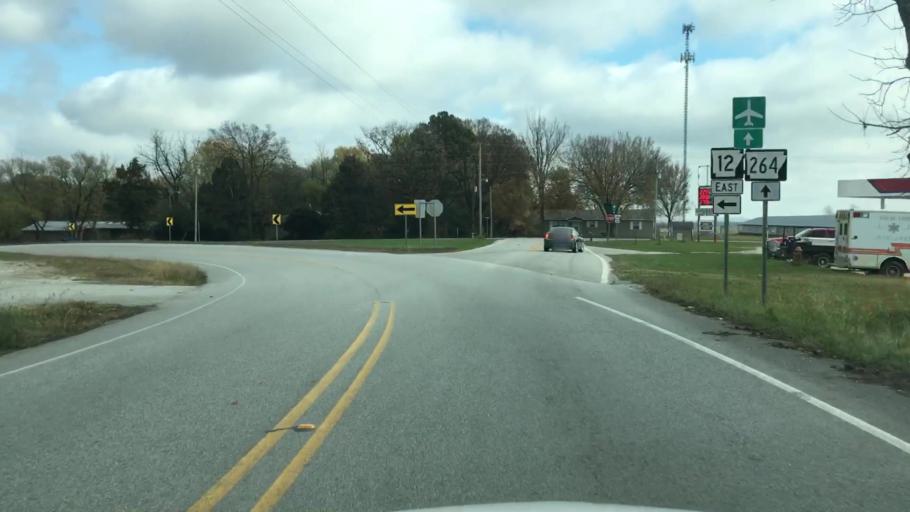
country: US
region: Arkansas
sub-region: Benton County
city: Centerton
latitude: 36.2616
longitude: -94.3517
